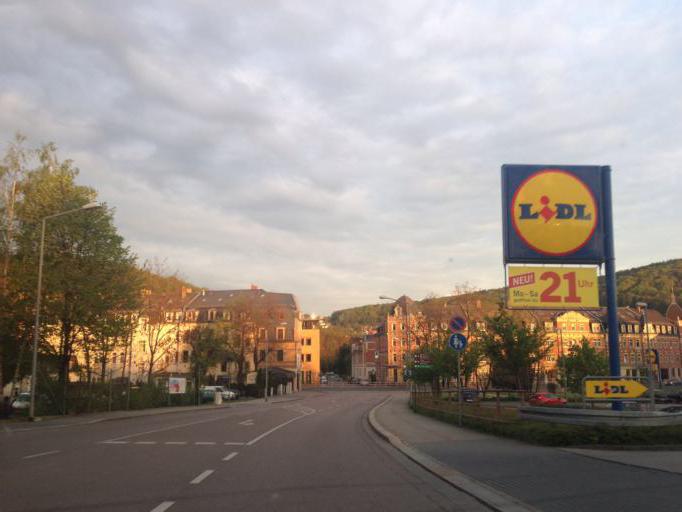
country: DE
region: Saxony
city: Freital
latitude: 51.0093
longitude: 13.6573
